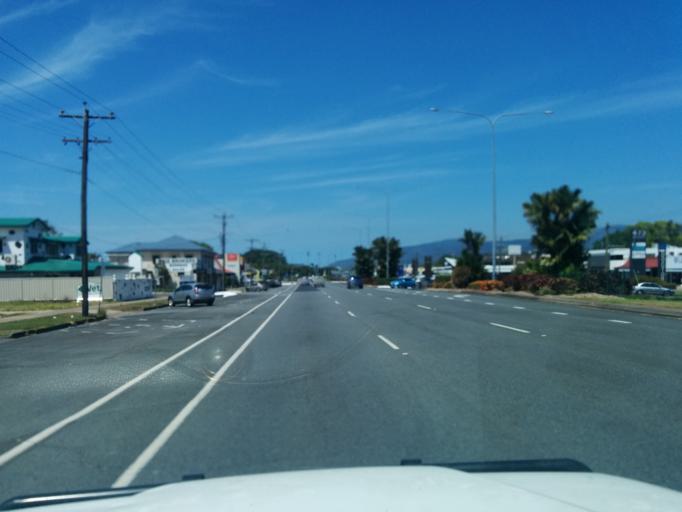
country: AU
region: Queensland
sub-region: Cairns
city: Woree
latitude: -16.9416
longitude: 145.7404
